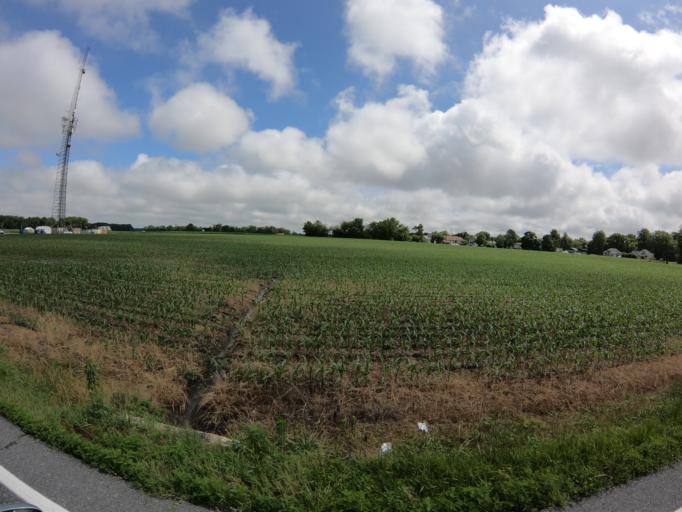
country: US
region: Maryland
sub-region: Caroline County
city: Greensboro
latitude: 39.0384
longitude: -75.7870
